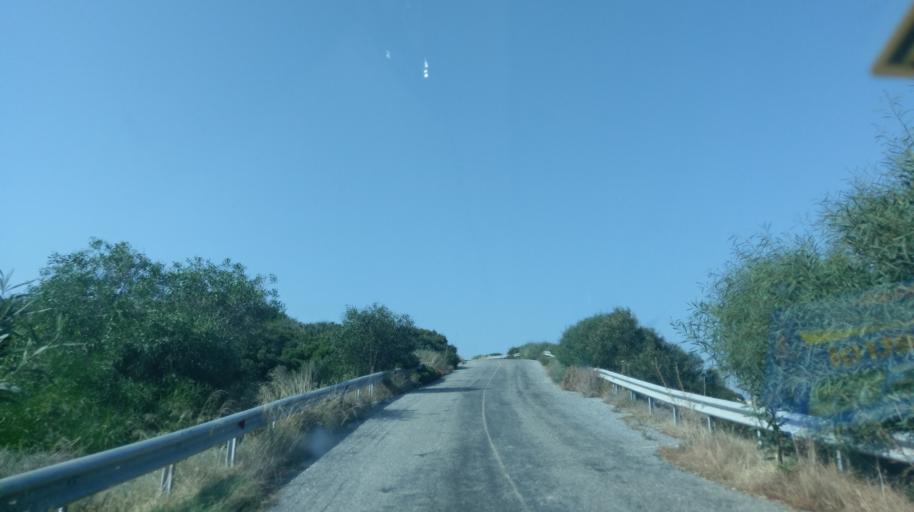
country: CY
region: Lefkosia
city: Morfou
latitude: 35.3670
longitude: 32.9913
